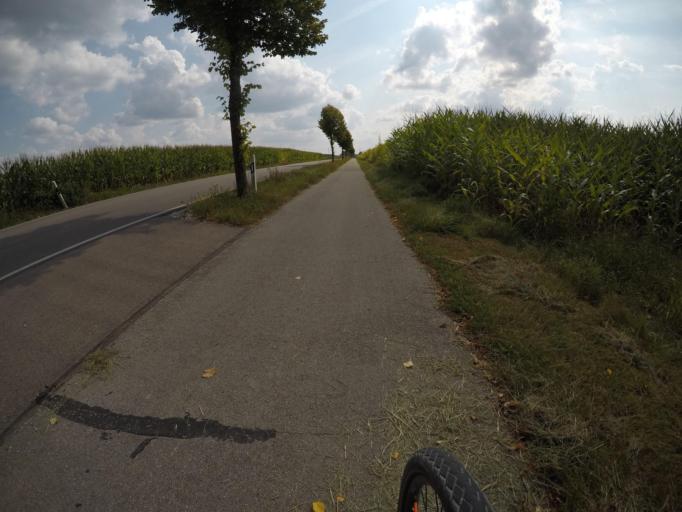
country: DE
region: Bavaria
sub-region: Swabia
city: Westendorf
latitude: 48.5616
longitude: 10.8436
